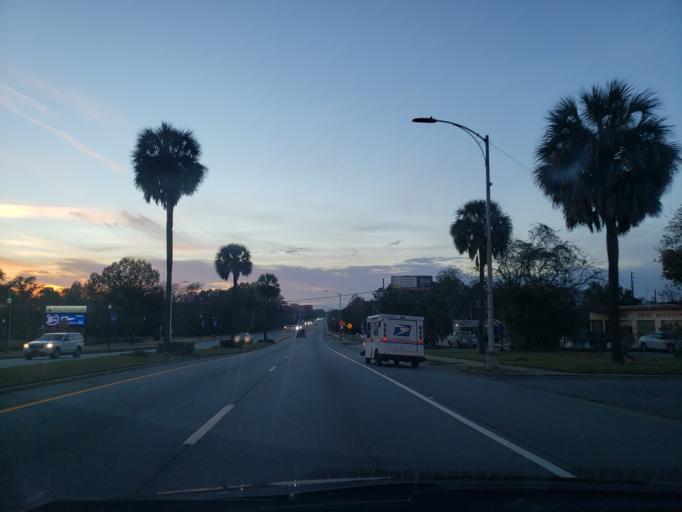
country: US
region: Georgia
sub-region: Dougherty County
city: Albany
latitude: 31.5757
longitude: -84.1442
